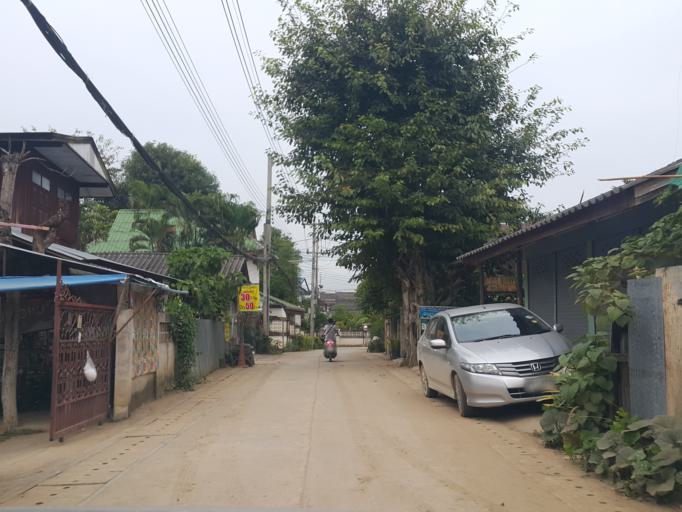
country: TH
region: Chiang Mai
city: Pai
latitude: 19.3587
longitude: 98.4426
